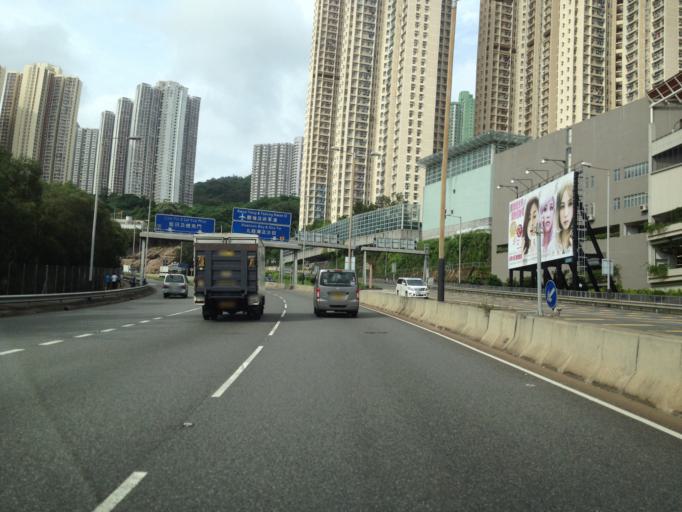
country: HK
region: Kowloon City
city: Kowloon
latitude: 22.3013
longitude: 114.2341
